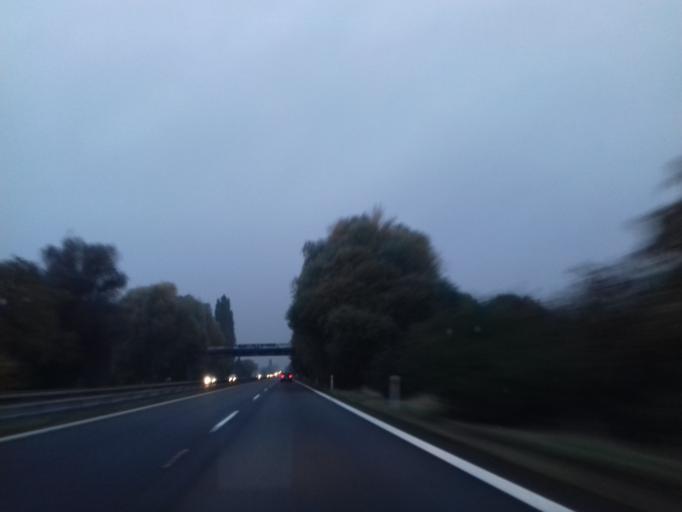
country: CZ
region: Olomoucky
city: Skrben
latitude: 49.6186
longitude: 17.1823
